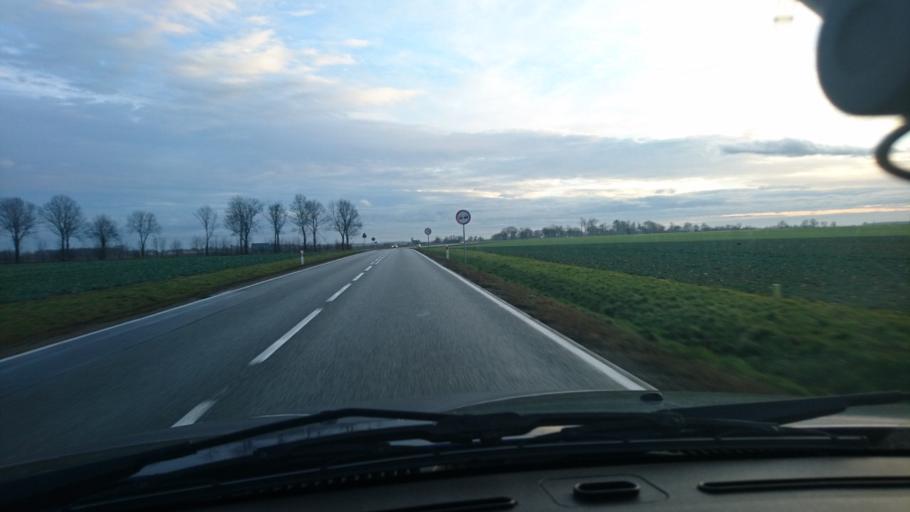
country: PL
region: Opole Voivodeship
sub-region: Powiat kluczborski
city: Byczyna
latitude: 51.0719
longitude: 18.2032
